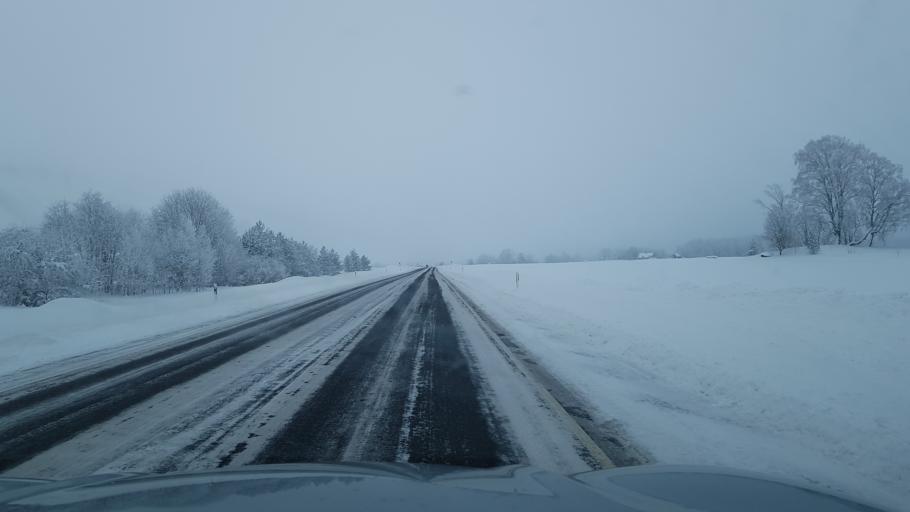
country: EE
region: Ida-Virumaa
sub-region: Johvi vald
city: Johvi
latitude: 59.2468
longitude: 27.3691
